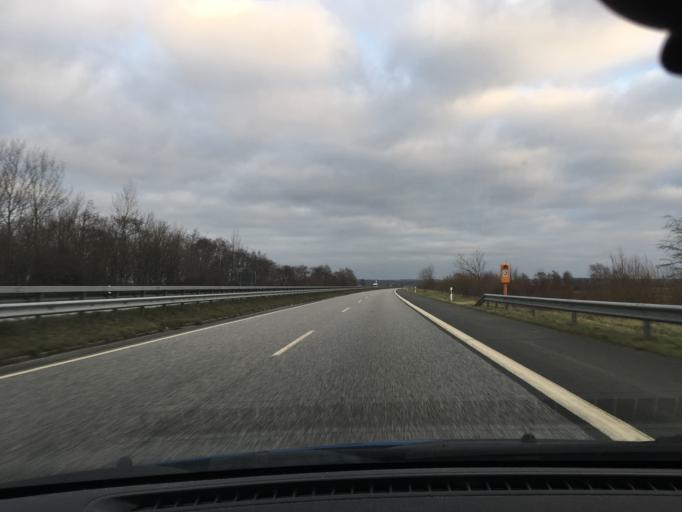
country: DE
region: Schleswig-Holstein
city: Heide
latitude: 54.1674
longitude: 9.1221
